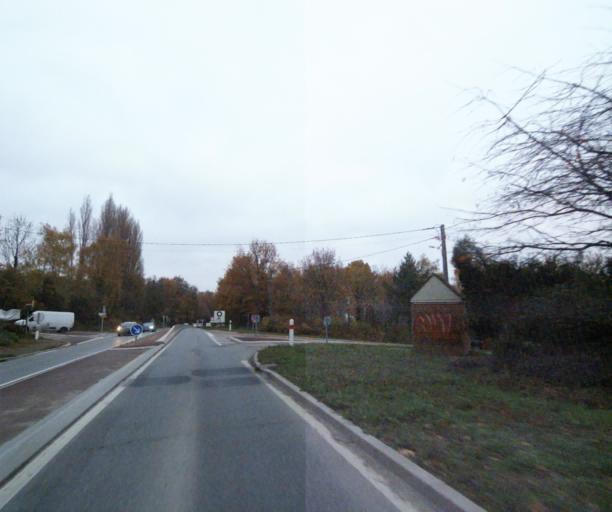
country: FR
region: Ile-de-France
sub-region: Departement des Yvelines
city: Villennes-sur-Seine
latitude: 48.9502
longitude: 1.9791
